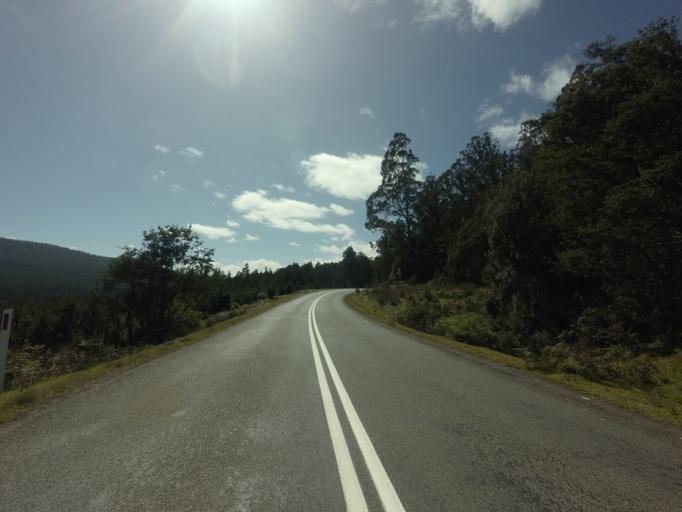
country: AU
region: Tasmania
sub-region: Derwent Valley
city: New Norfolk
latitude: -42.7410
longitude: 146.6585
